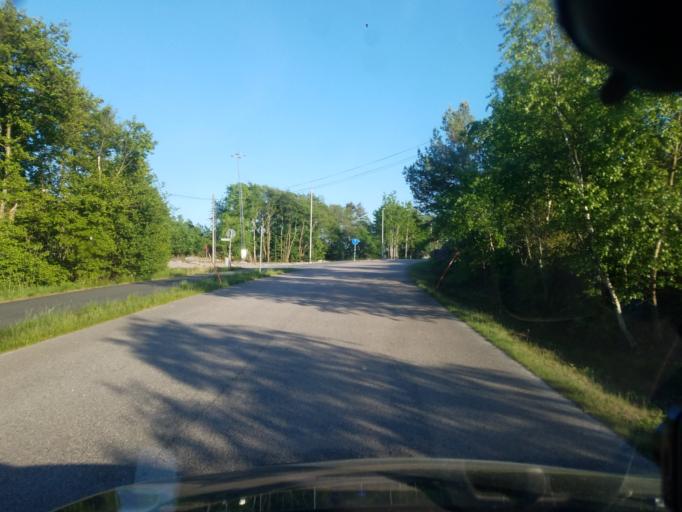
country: SE
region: Vaestra Goetaland
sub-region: Lysekils Kommun
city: Lysekil
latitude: 58.2912
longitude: 11.4566
